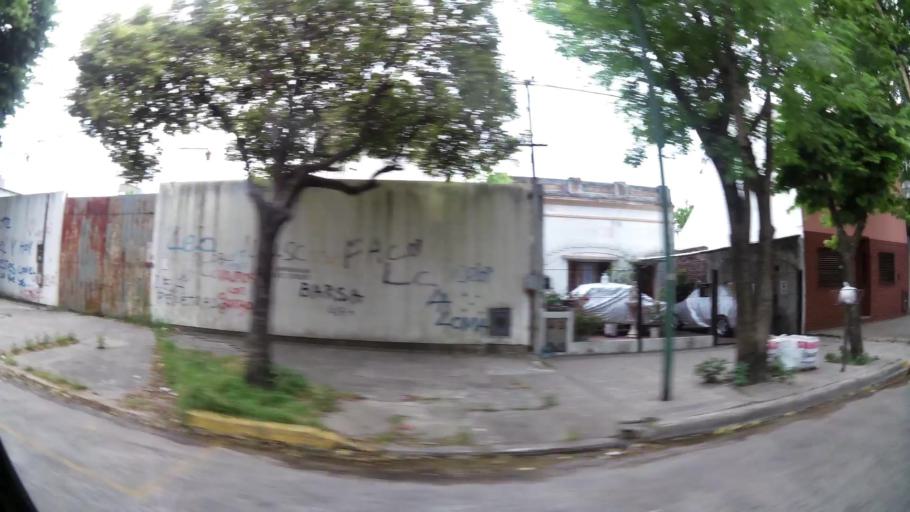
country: AR
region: Buenos Aires
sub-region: Partido de La Plata
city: La Plata
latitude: -34.9231
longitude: -57.9834
